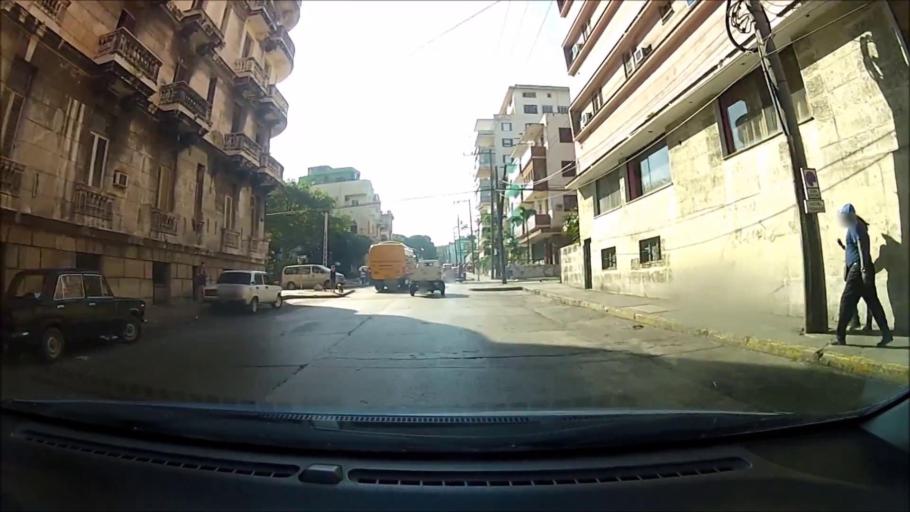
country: CU
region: La Habana
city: Havana
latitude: 23.1404
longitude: -82.3797
